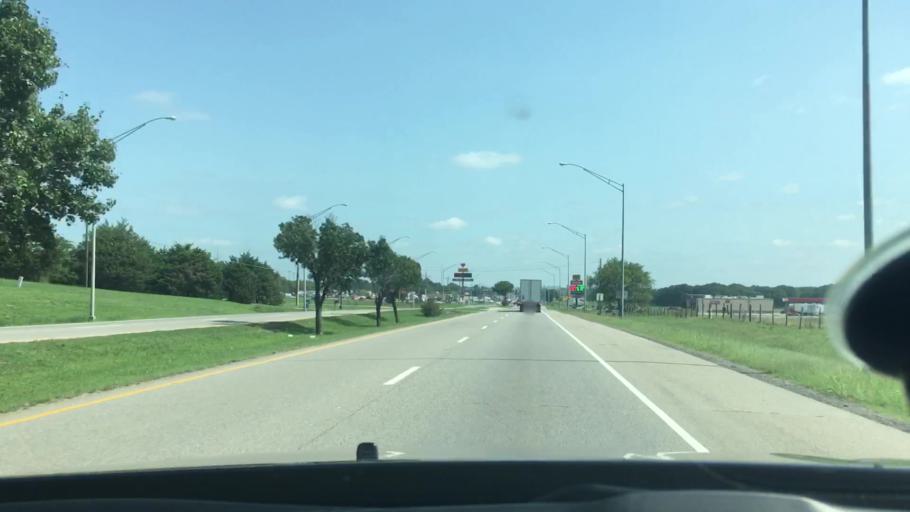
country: US
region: Oklahoma
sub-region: Atoka County
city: Atoka
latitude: 34.3620
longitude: -96.1434
